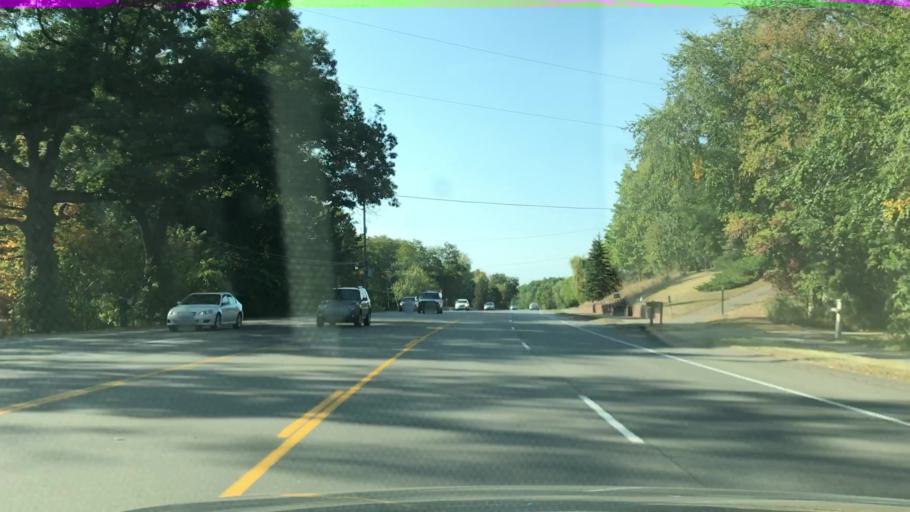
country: US
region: Michigan
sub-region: Kent County
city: Forest Hills
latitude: 42.9299
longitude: -85.5203
